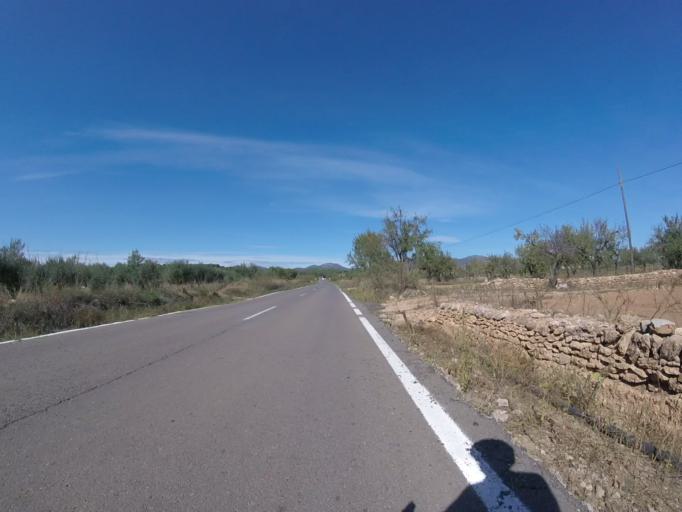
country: ES
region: Valencia
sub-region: Provincia de Castello
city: Benlloch
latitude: 40.2175
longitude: 0.0176
